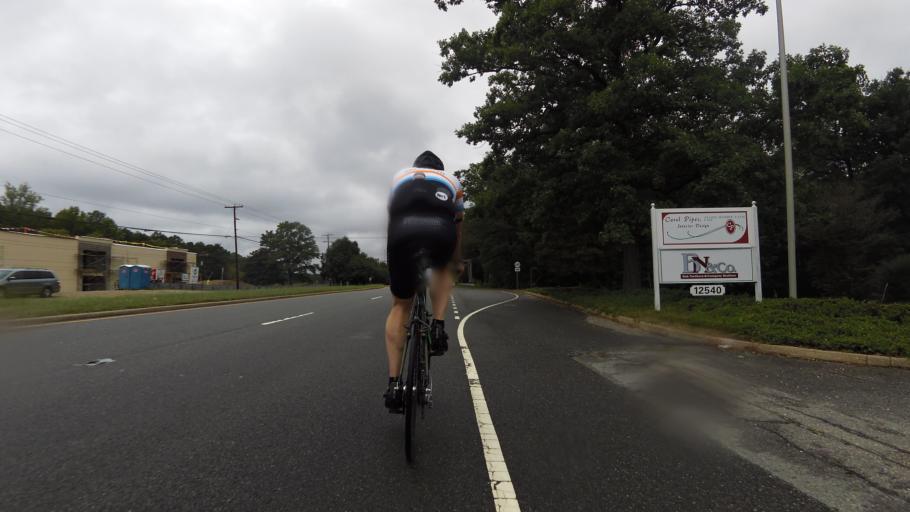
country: US
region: Virginia
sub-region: Henrico County
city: Short Pump
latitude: 37.5992
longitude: -77.6492
